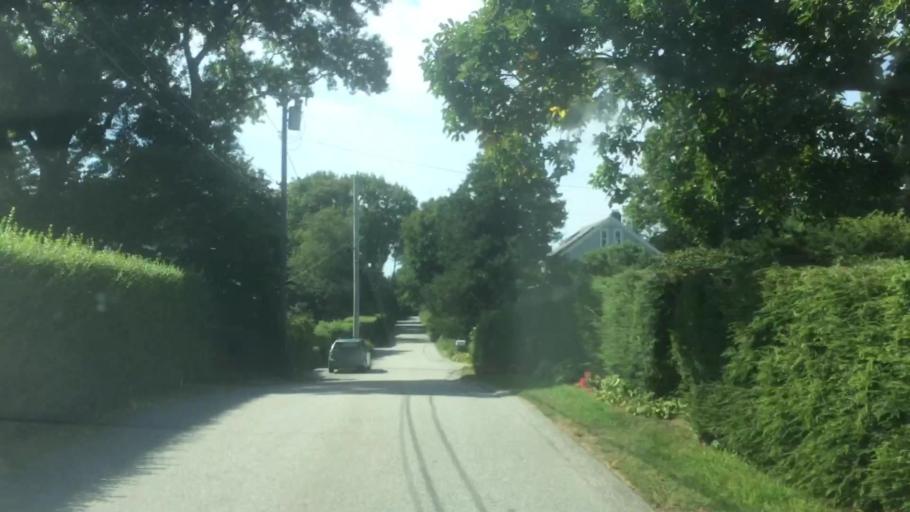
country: US
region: Rhode Island
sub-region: Newport County
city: Jamestown
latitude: 41.5083
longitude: -71.4192
